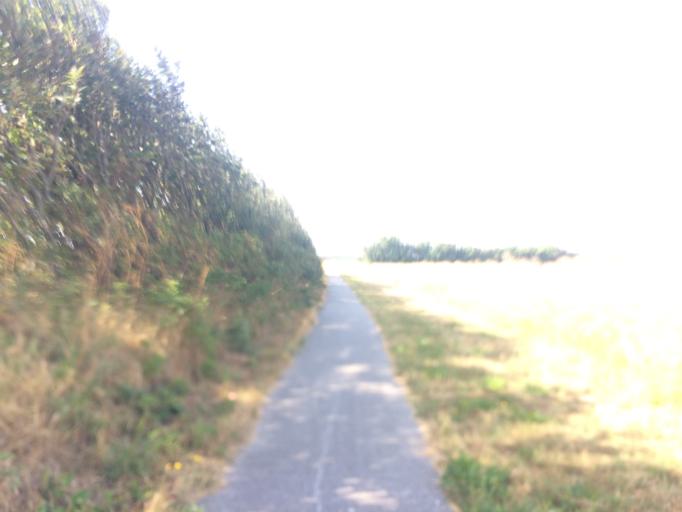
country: DK
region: Central Jutland
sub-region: Holstebro Kommune
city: Vinderup
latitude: 56.6367
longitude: 8.7890
